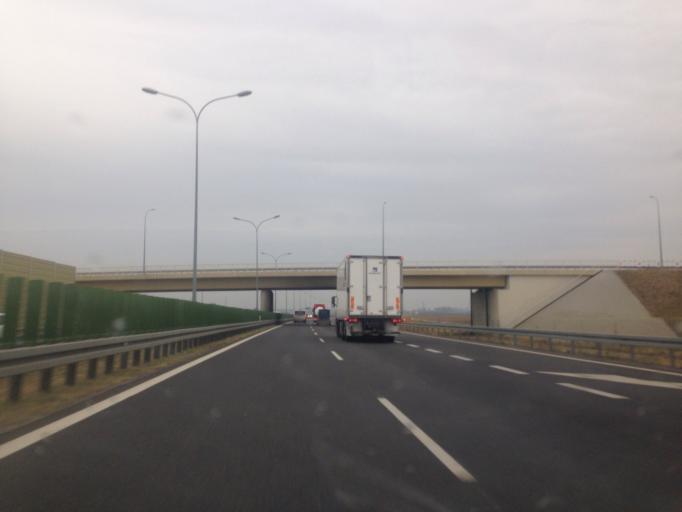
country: PL
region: Greater Poland Voivodeship
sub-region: Powiat poznanski
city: Kostrzyn
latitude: 52.3820
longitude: 17.2428
